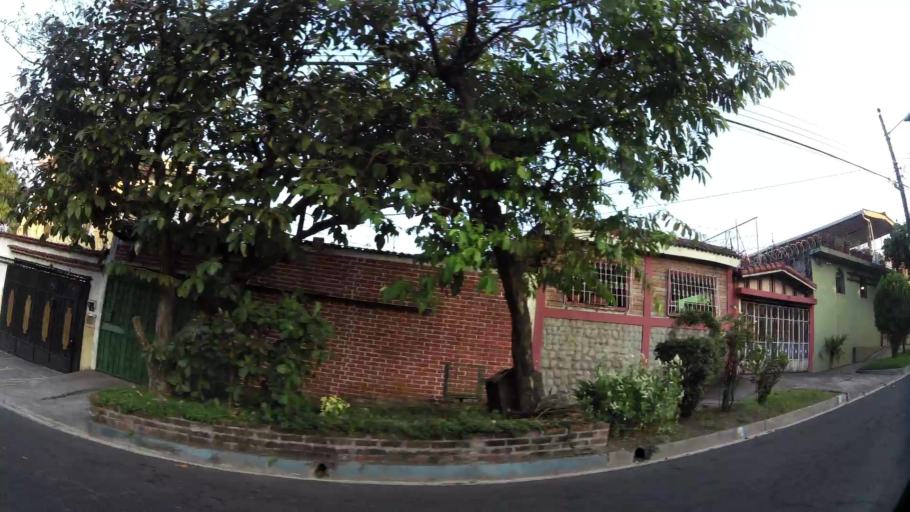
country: SV
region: San Salvador
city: San Salvador
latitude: 13.6836
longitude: -89.2105
